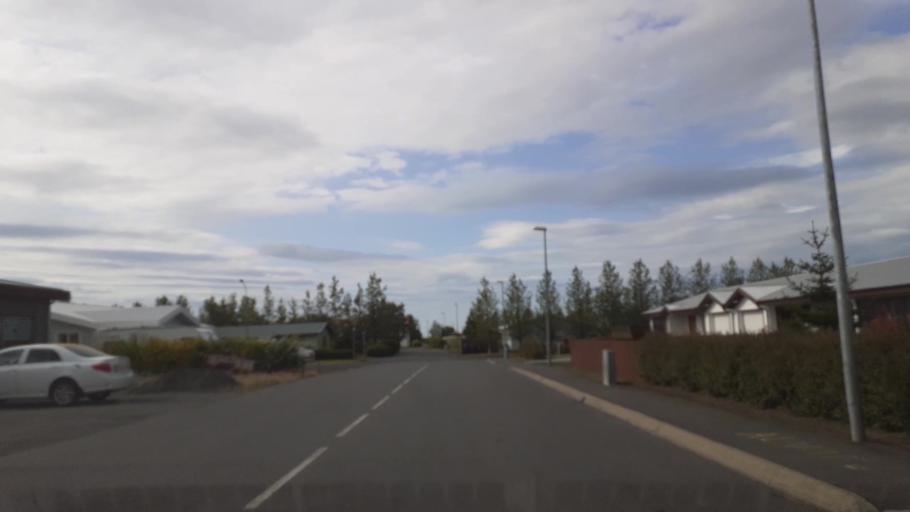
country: IS
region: South
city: Vestmannaeyjar
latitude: 63.8344
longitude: -20.3890
